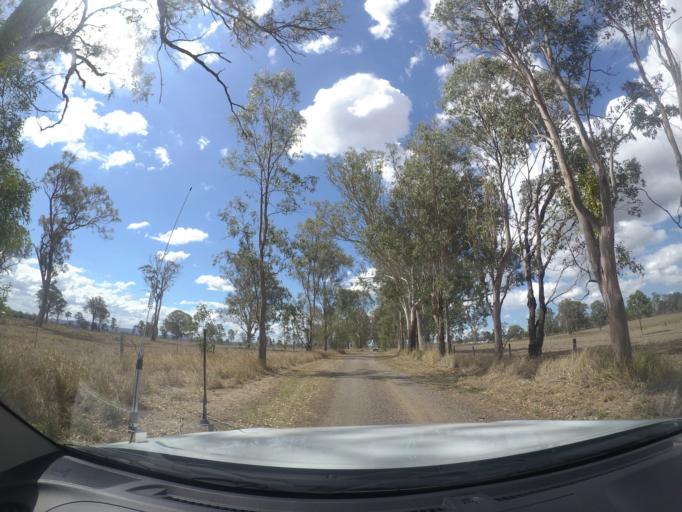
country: AU
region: Queensland
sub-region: Logan
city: Cedar Vale
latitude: -27.8837
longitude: 152.9608
